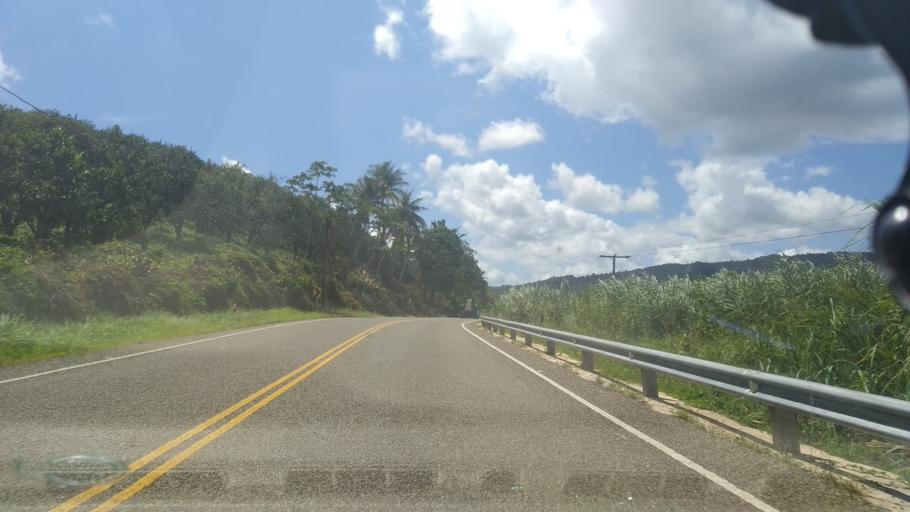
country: BZ
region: Stann Creek
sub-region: Dangriga
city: Dangriga
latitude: 17.0371
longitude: -88.5225
